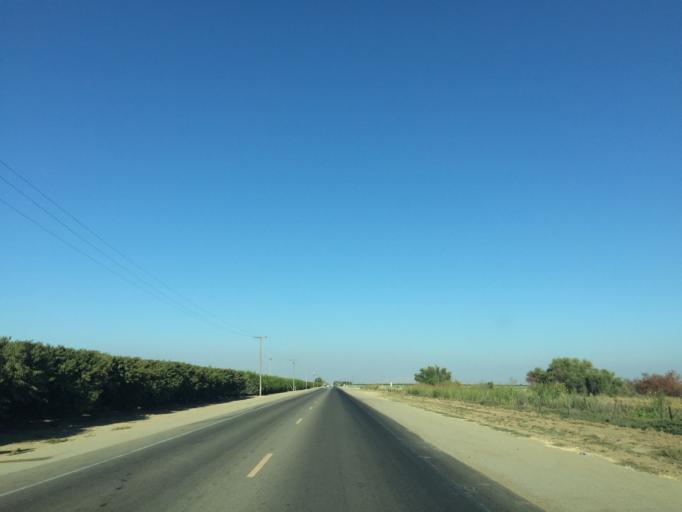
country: US
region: California
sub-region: Tulare County
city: London
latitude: 36.4884
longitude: -119.4478
